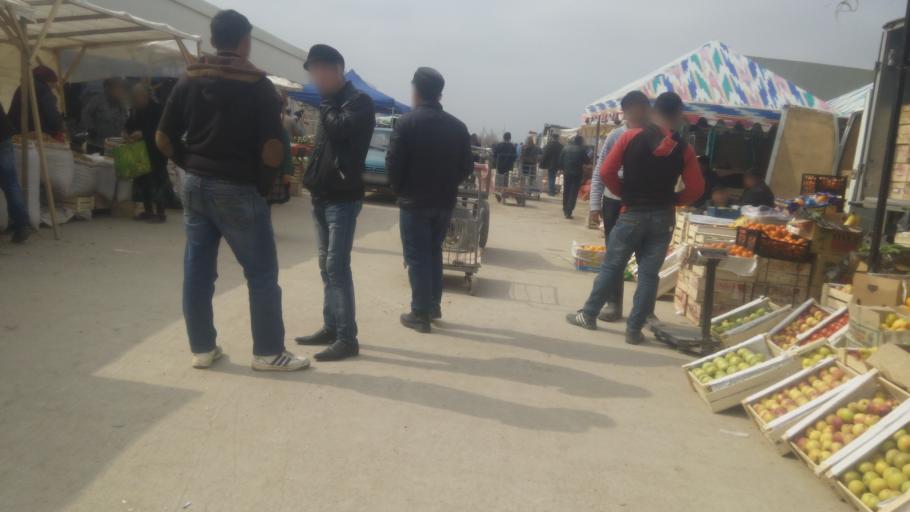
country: UZ
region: Sirdaryo
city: Guliston
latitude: 40.4768
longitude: 68.7799
